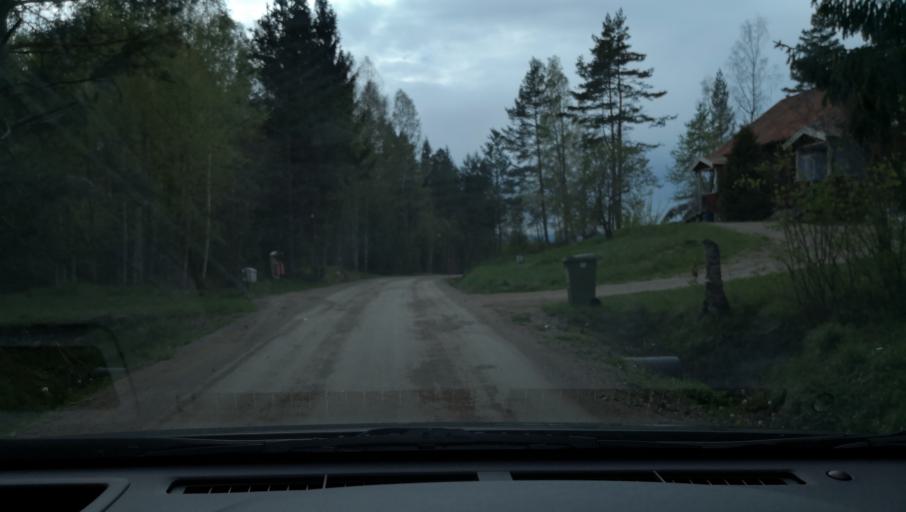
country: SE
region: Vaestmanland
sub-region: Fagersta Kommun
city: Fagersta
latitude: 60.1211
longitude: 15.6892
